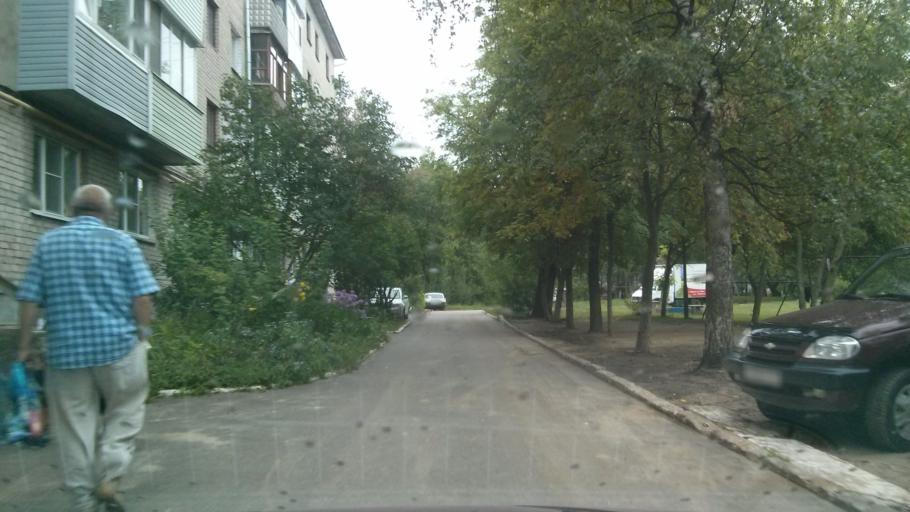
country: RU
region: Vladimir
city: Murom
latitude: 55.5488
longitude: 42.0564
